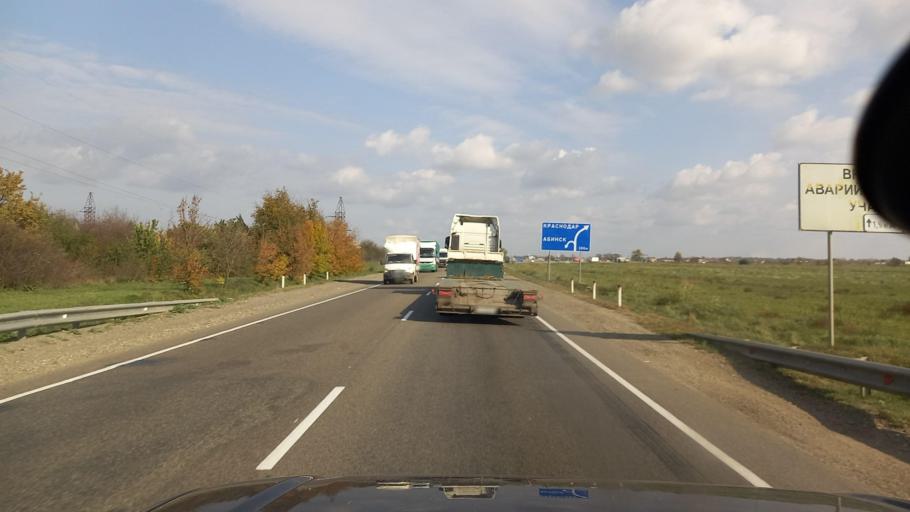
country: RU
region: Krasnodarskiy
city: Abinsk
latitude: 44.8546
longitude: 38.1870
